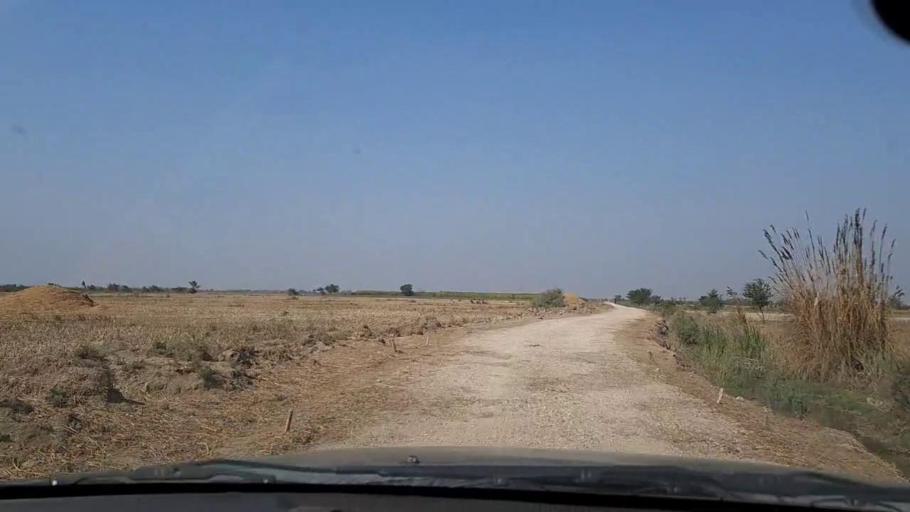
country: PK
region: Sindh
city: Mirpur Sakro
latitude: 24.3624
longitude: 67.6830
